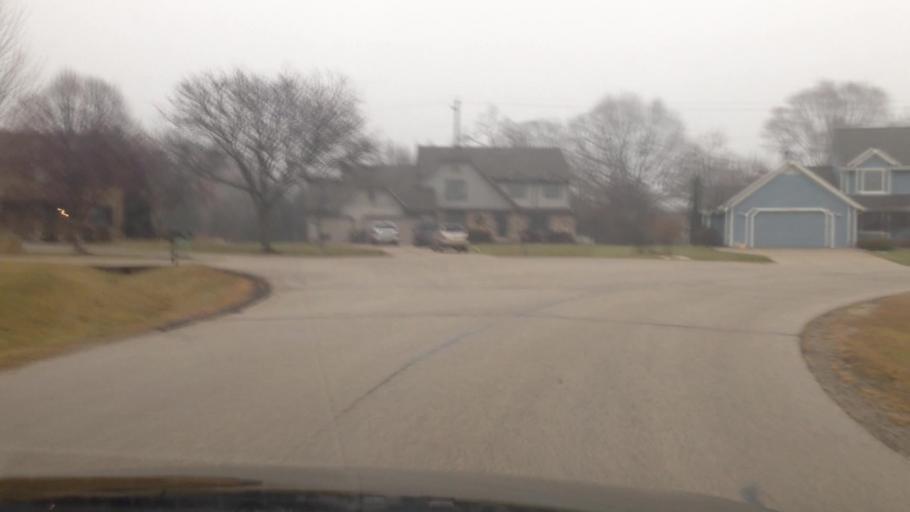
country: US
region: Wisconsin
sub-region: Waukesha County
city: Muskego
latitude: 42.9112
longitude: -88.0909
